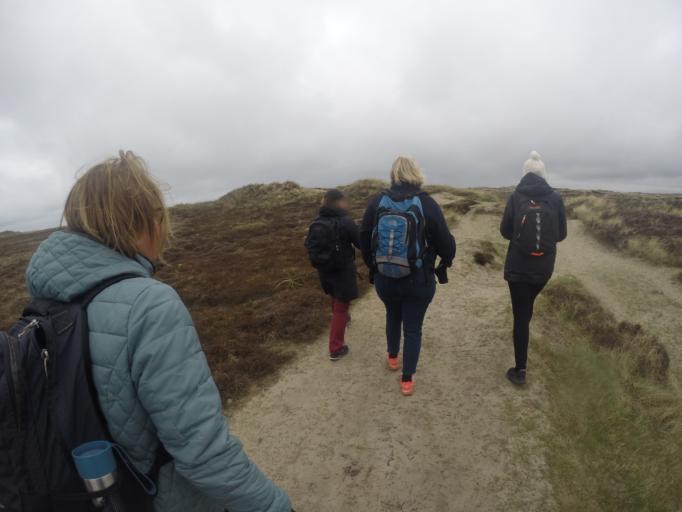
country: DK
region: Central Jutland
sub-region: Lemvig Kommune
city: Thyboron
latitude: 56.8269
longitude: 8.2630
